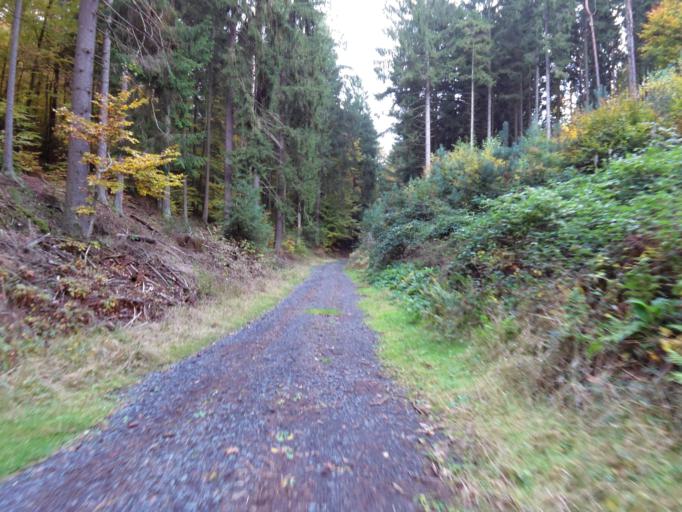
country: DE
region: Rheinland-Pfalz
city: Weidenthal
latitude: 49.4478
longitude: 8.0178
